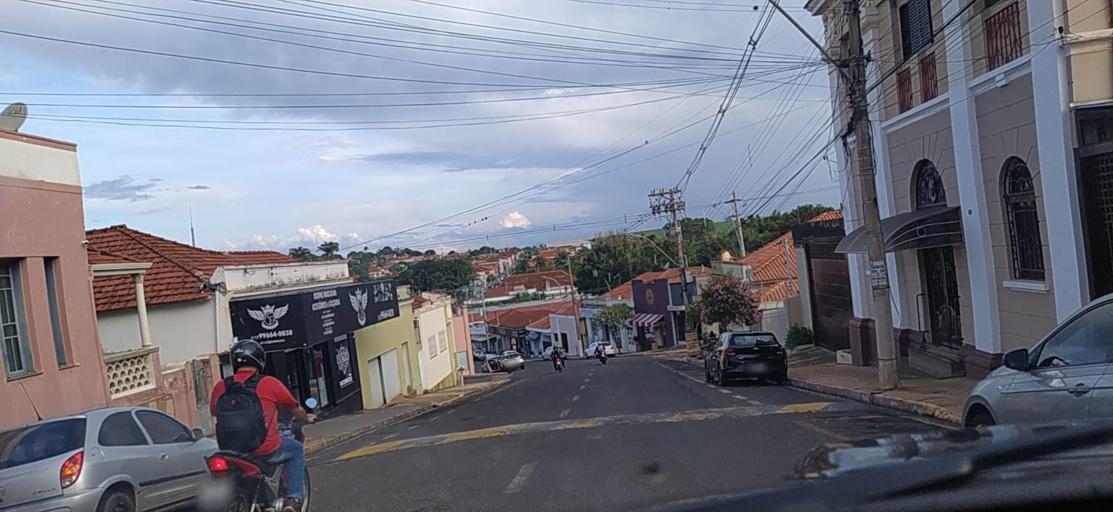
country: BR
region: Sao Paulo
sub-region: Pindorama
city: Pindorama
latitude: -21.1875
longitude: -48.9069
